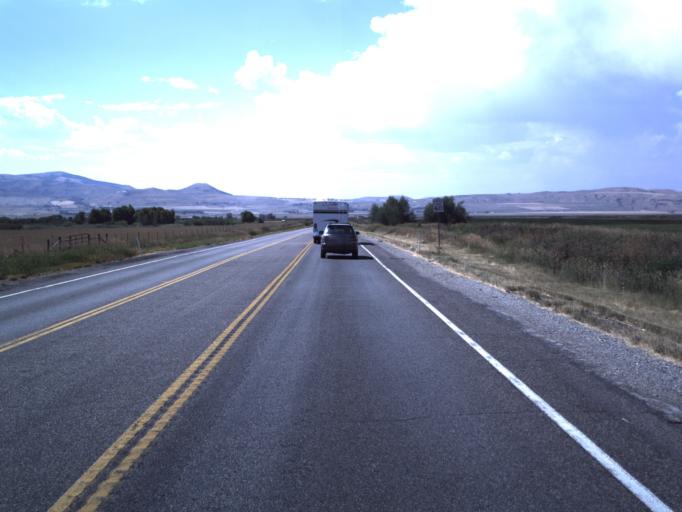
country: US
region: Utah
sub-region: Cache County
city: Benson
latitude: 41.7420
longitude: -111.9130
